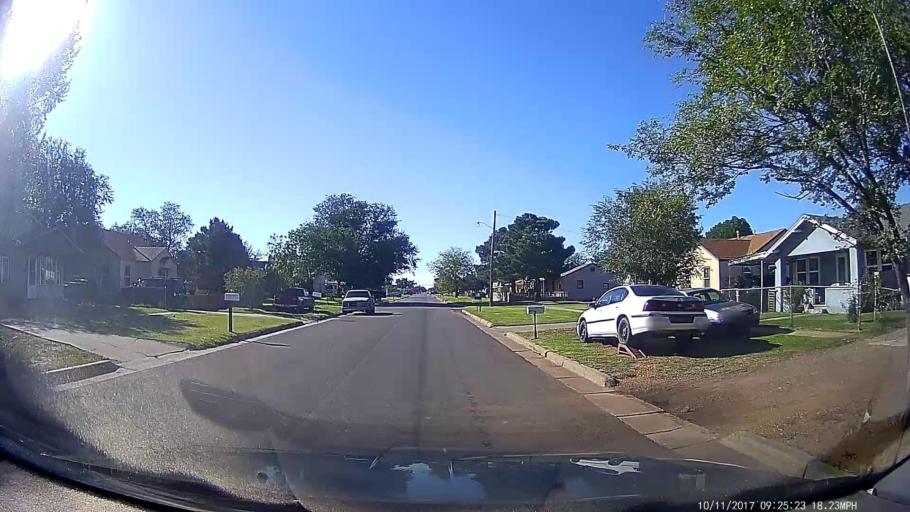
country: US
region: New Mexico
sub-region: Curry County
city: Clovis
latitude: 34.4093
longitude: -103.2103
